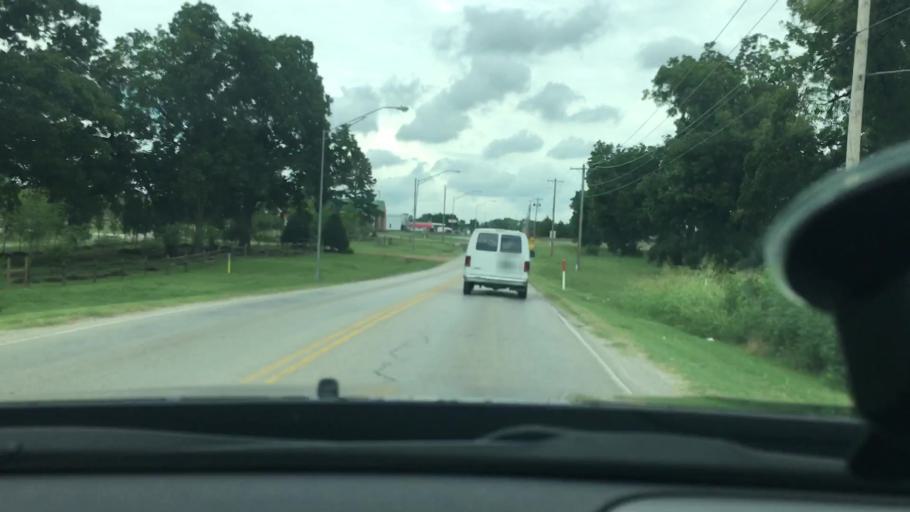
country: US
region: Oklahoma
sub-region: Carter County
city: Ardmore
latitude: 34.1754
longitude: -97.1605
